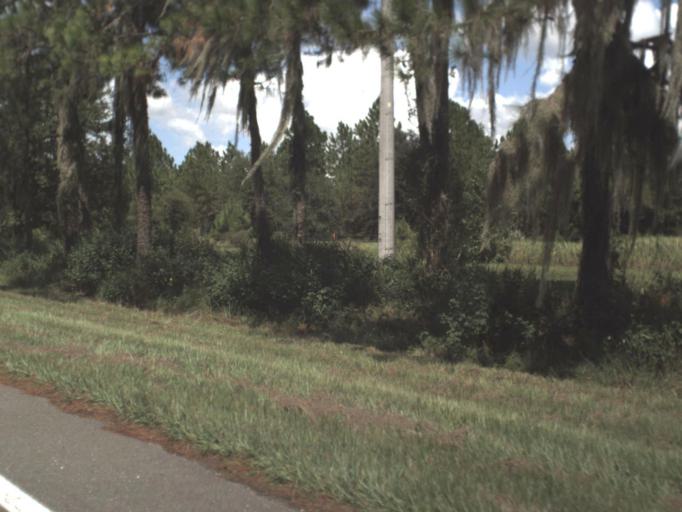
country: US
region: Florida
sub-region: Polk County
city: Mulberry
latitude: 27.7048
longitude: -82.0469
